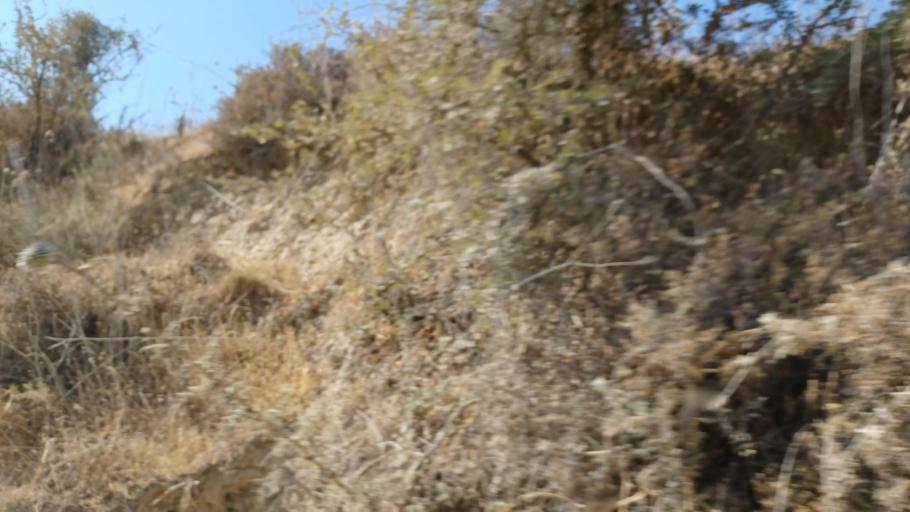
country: CY
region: Pafos
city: Tala
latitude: 34.9315
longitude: 32.4837
